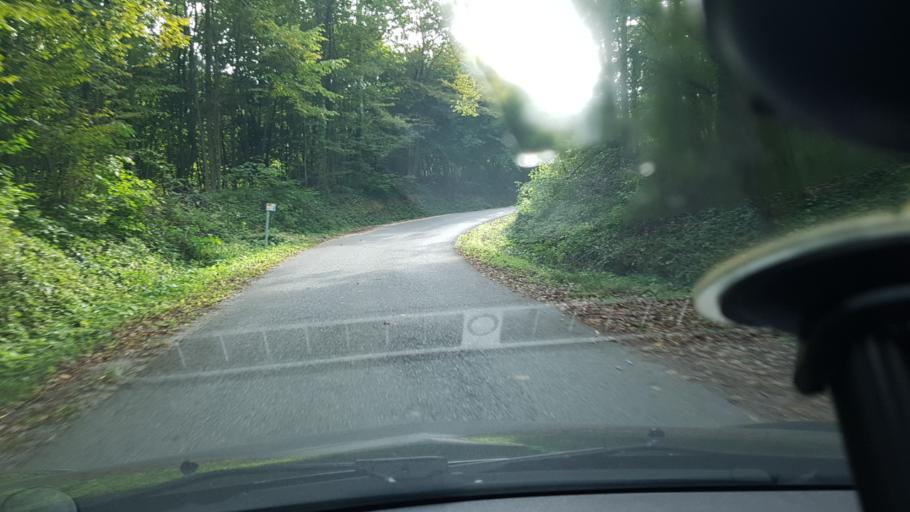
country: HR
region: Krapinsko-Zagorska
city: Radoboj
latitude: 46.1778
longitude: 15.9639
